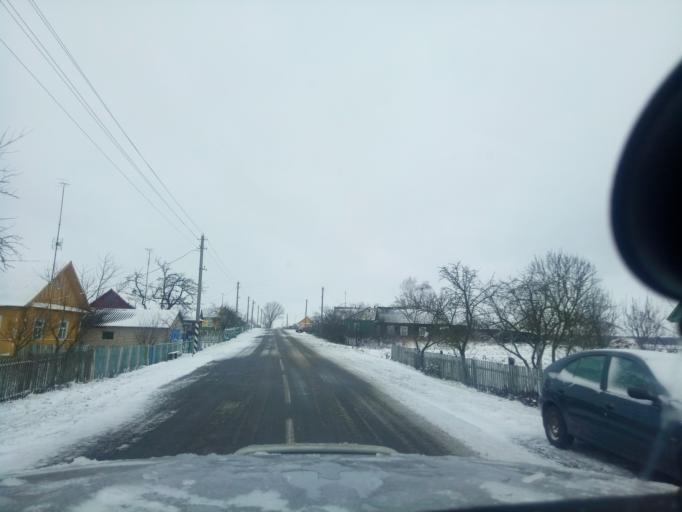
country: BY
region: Minsk
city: Klyetsk
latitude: 53.0091
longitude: 26.7017
